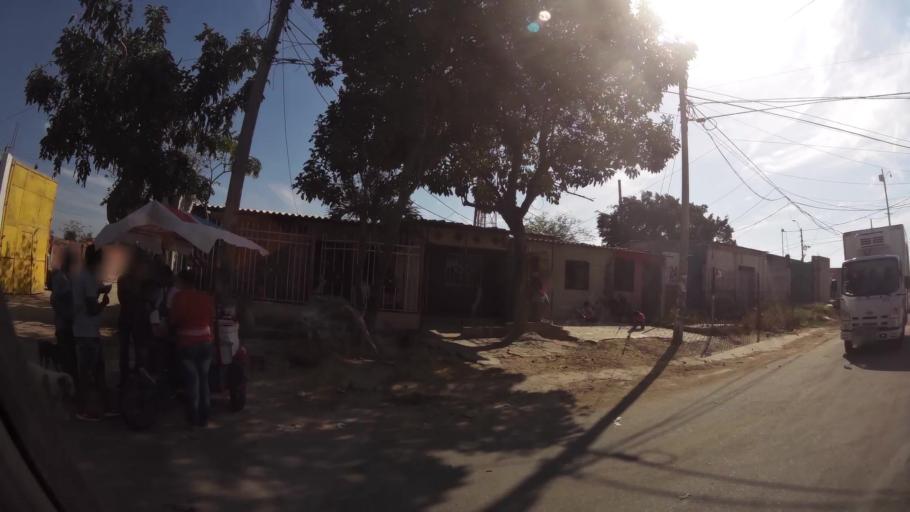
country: CO
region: Atlantico
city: Soledad
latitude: 10.9245
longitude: -74.8161
